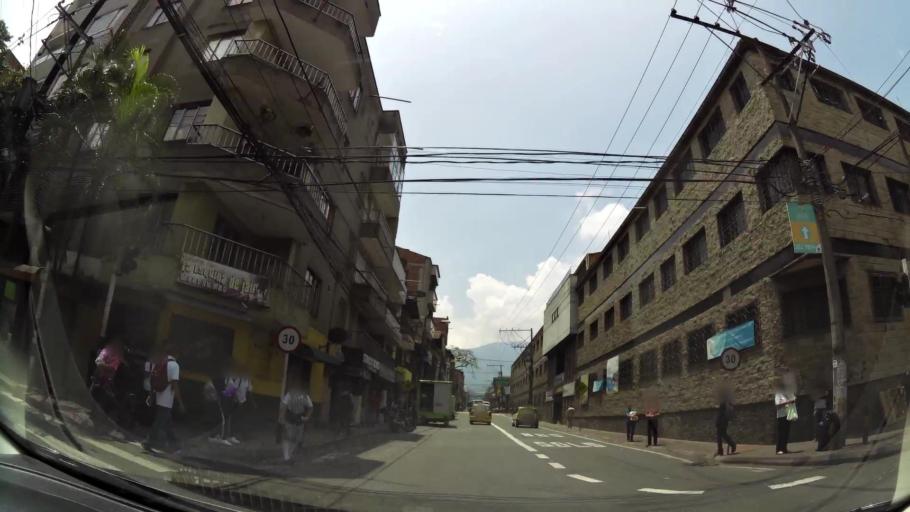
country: CO
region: Antioquia
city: Itagui
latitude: 6.1731
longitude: -75.6111
